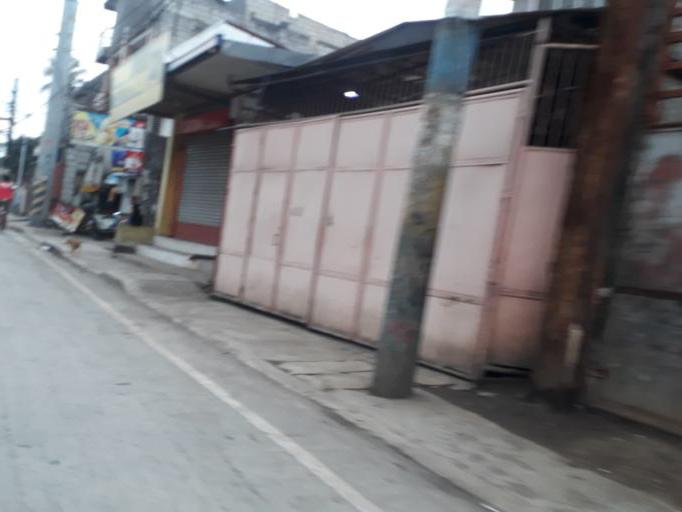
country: PH
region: Calabarzon
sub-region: Province of Rizal
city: Valenzuela
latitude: 14.6852
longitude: 120.9583
